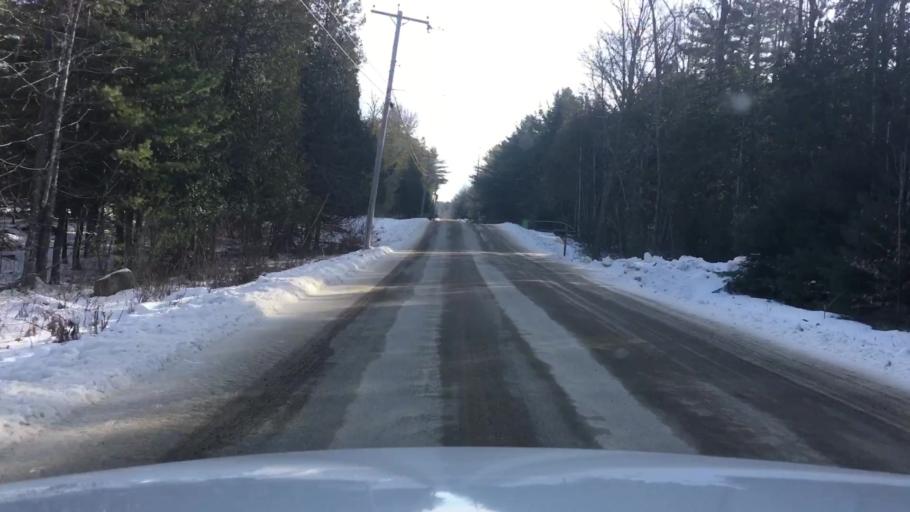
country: US
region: Maine
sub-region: Penobscot County
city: Holden
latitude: 44.7733
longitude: -68.5846
